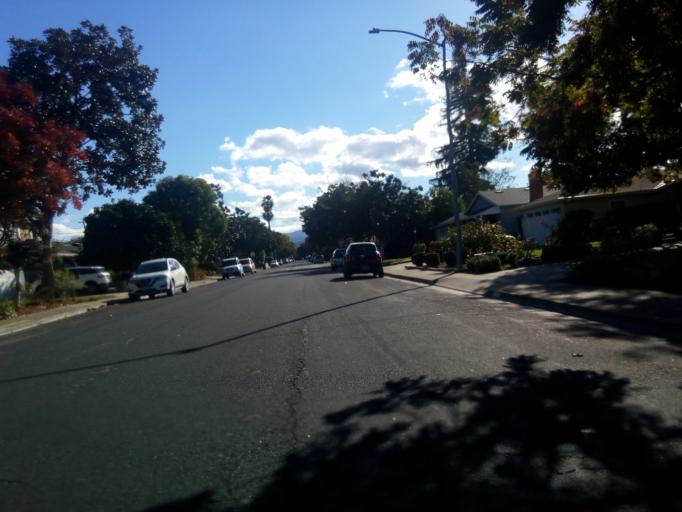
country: US
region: California
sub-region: Santa Clara County
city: Mountain View
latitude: 37.3781
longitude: -122.0852
